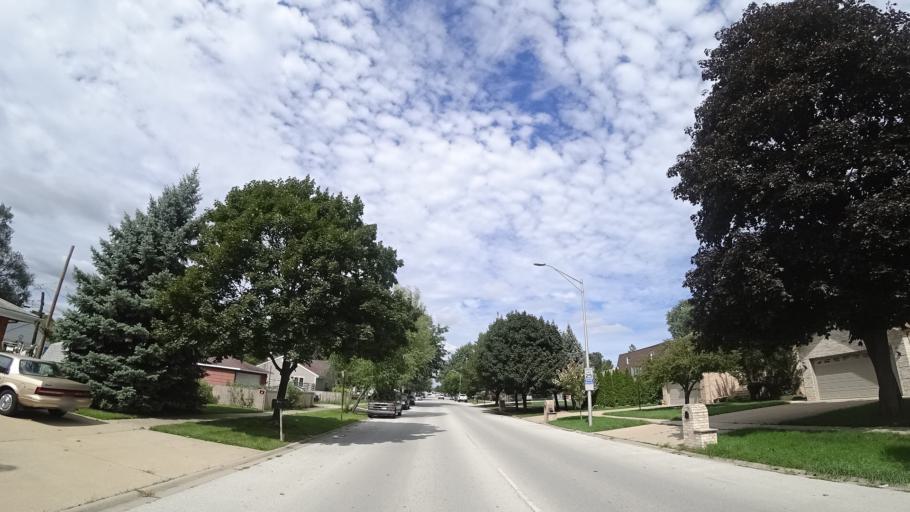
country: US
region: Illinois
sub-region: Cook County
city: Chicago Ridge
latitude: 41.7160
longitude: -87.7896
